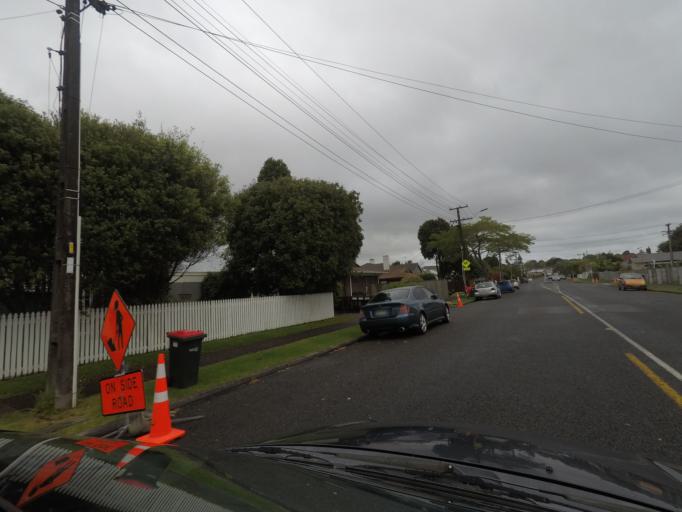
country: NZ
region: Auckland
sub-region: Auckland
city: Auckland
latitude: -36.8881
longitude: 174.7326
